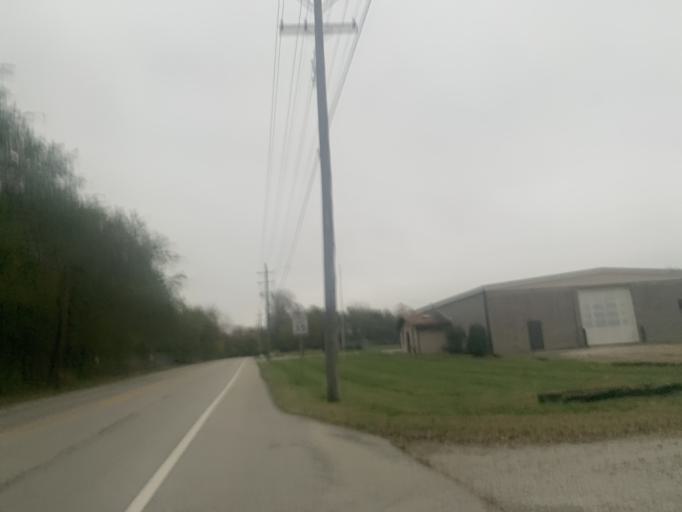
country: US
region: Kentucky
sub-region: Jefferson County
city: Shively
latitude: 38.2138
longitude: -85.8356
